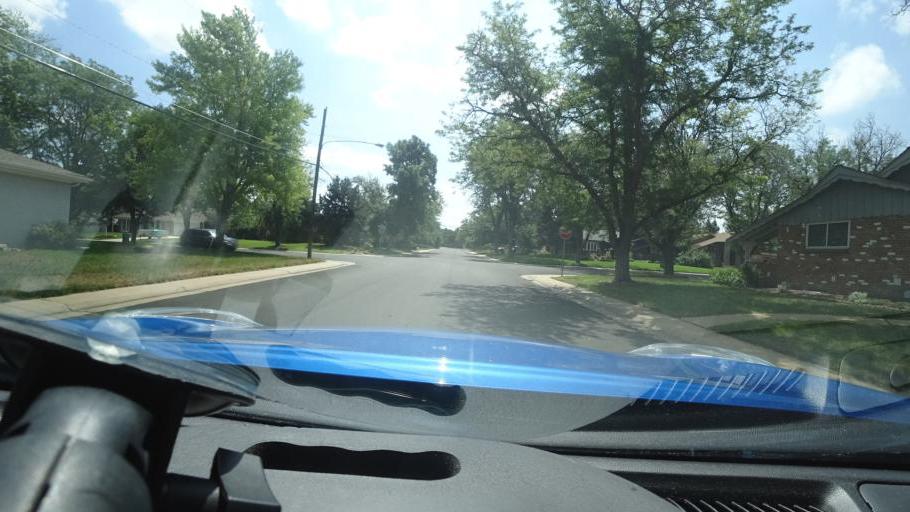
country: US
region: Colorado
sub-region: Adams County
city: Aurora
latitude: 39.7218
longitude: -104.8535
